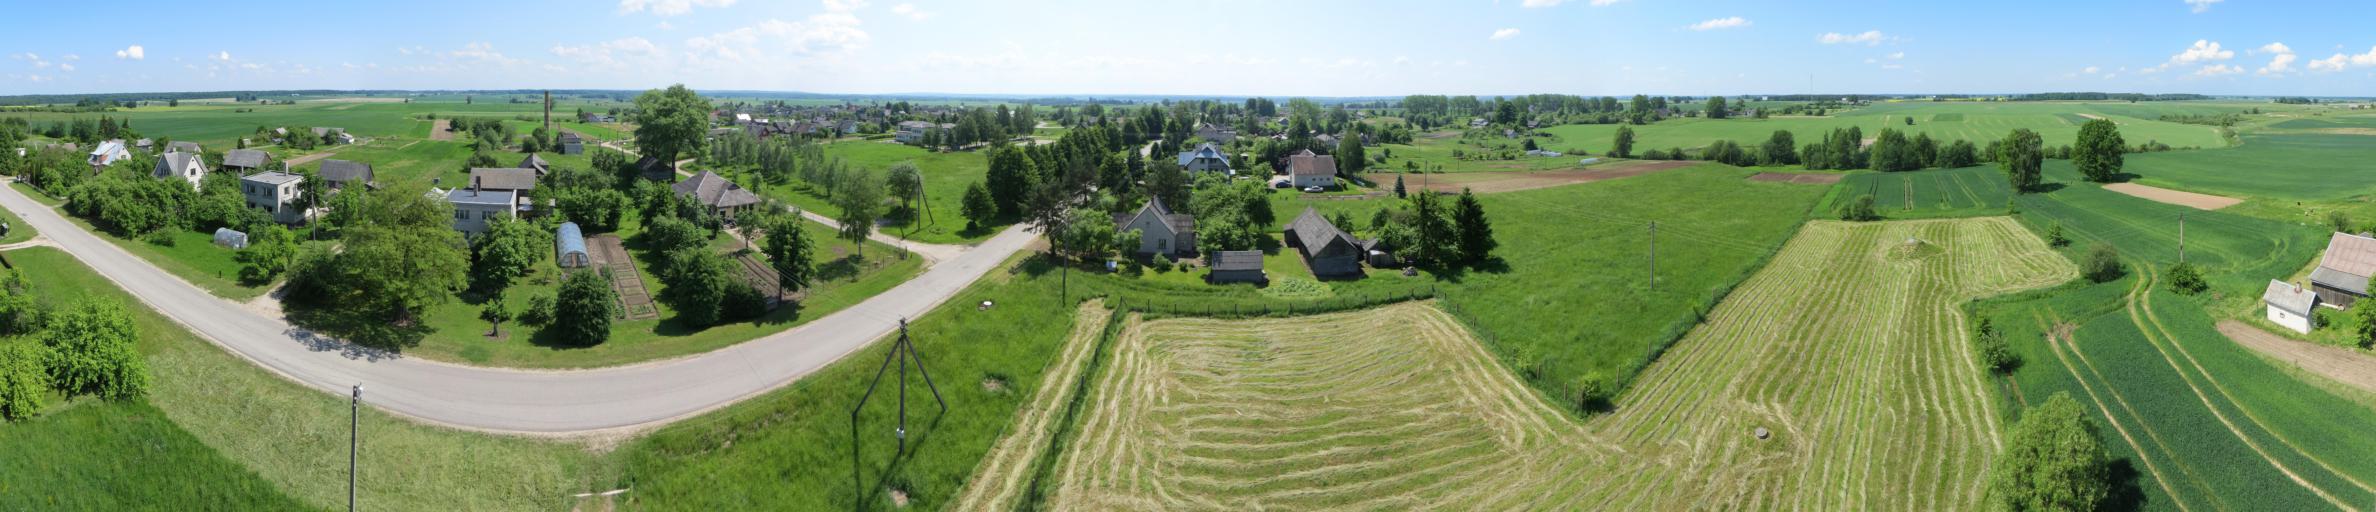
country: LT
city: Kaisiadorys
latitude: 54.8530
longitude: 24.3400
